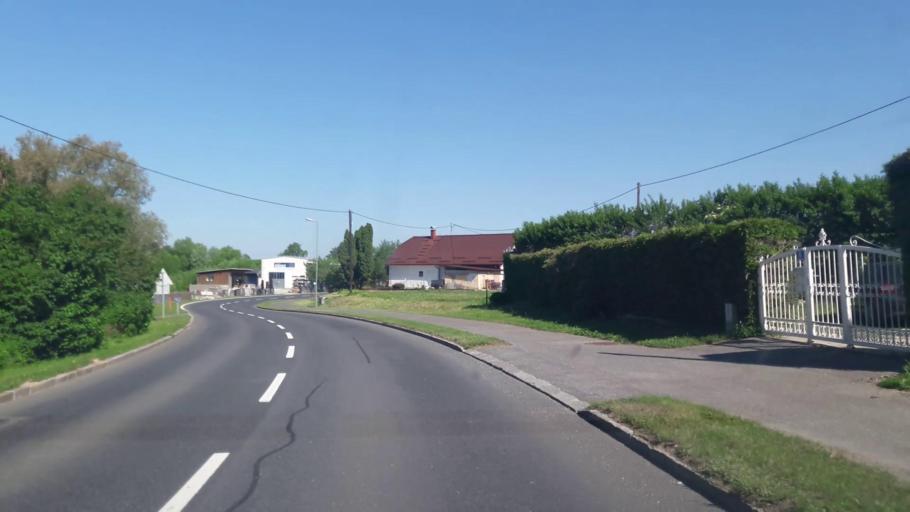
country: AT
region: Styria
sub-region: Politischer Bezirk Hartberg-Fuerstenfeld
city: Burgau
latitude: 47.1513
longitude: 16.1156
